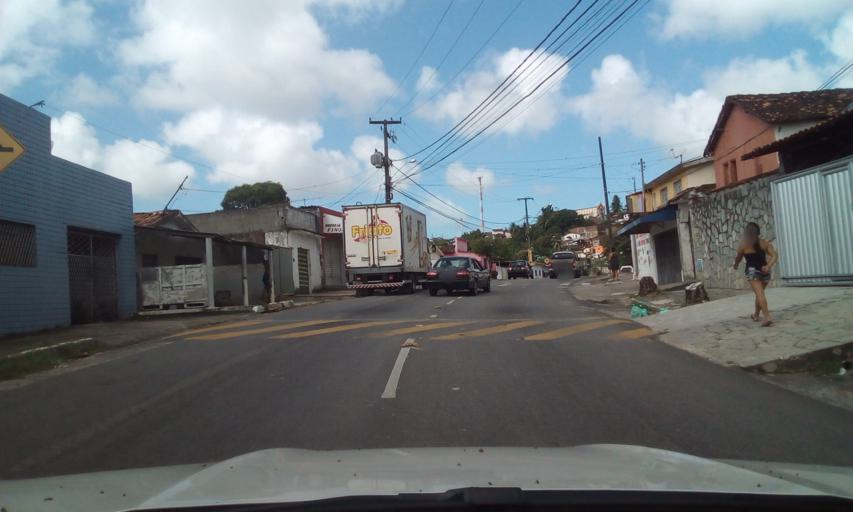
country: BR
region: Paraiba
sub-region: Joao Pessoa
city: Joao Pessoa
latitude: -7.1129
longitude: -34.8853
